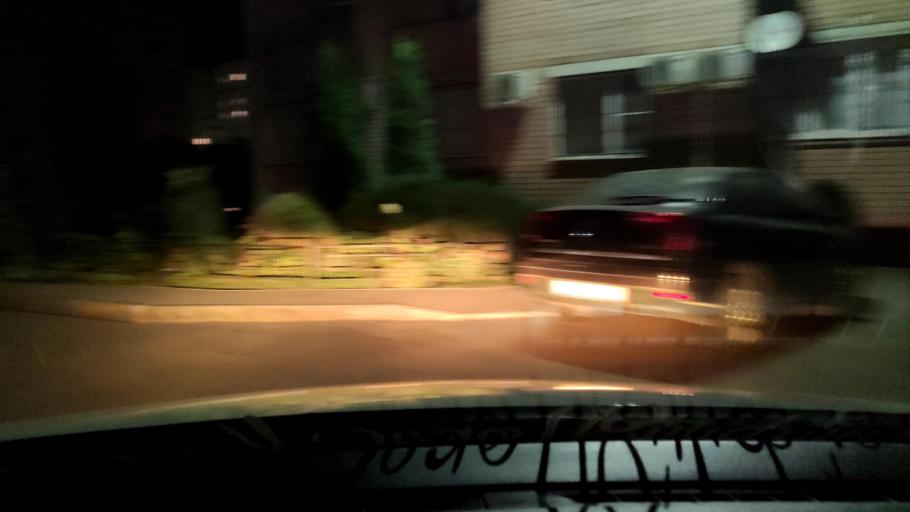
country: RU
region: Voronezj
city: Podgornoye
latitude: 51.7284
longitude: 39.2074
